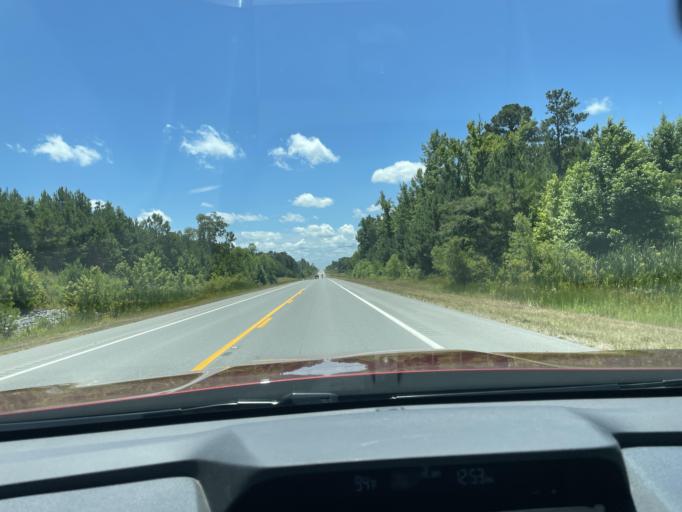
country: US
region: Arkansas
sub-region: Lincoln County
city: Star City
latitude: 33.9084
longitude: -91.8833
